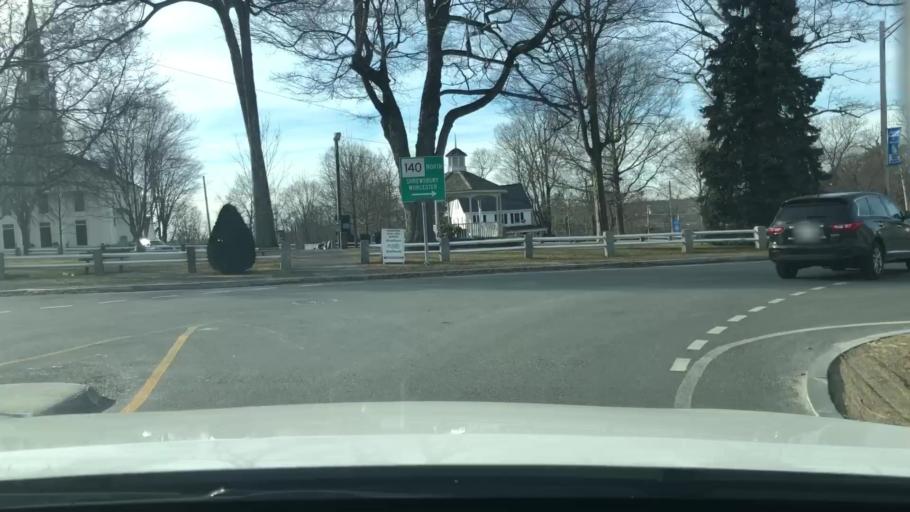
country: US
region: Massachusetts
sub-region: Worcester County
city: Grafton
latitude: 42.2063
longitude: -71.6849
